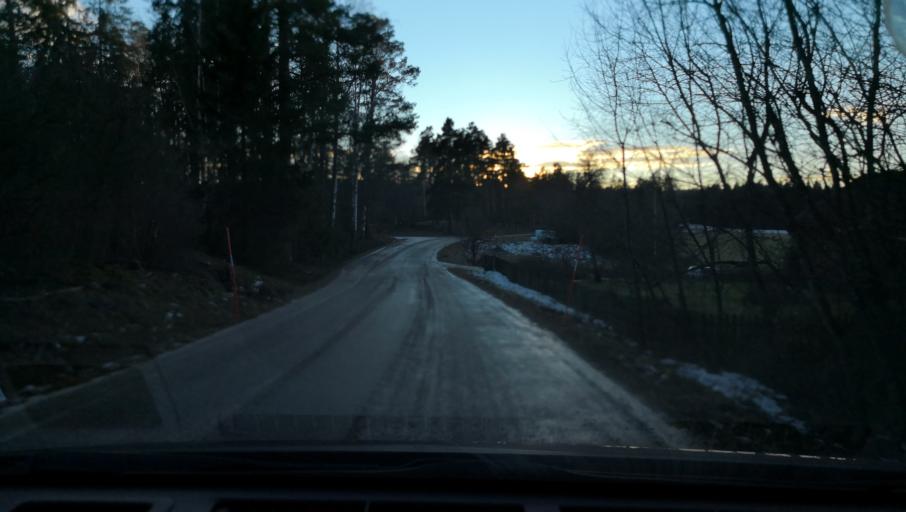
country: SE
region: Vaestmanland
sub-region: Vasteras
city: Tillberga
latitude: 59.7723
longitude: 16.6007
